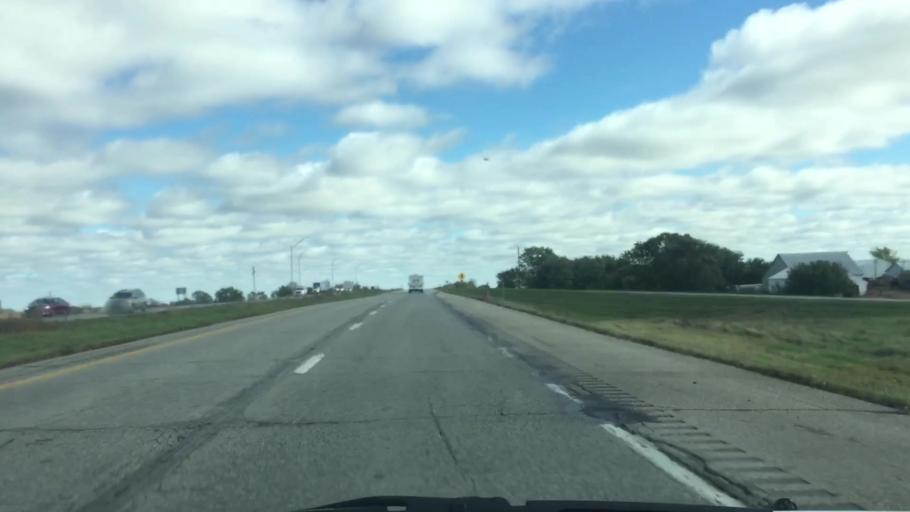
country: US
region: Iowa
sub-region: Poweshiek County
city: Grinnell
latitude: 41.6961
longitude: -92.7260
